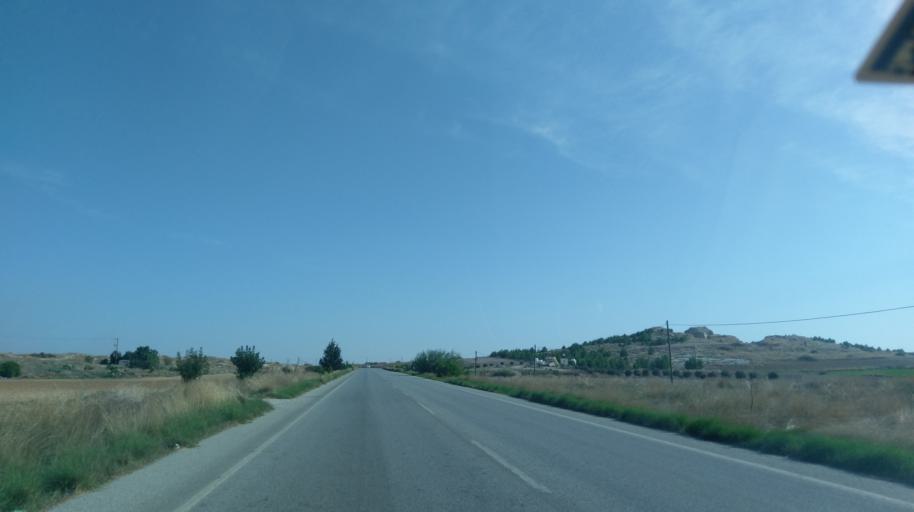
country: CY
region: Ammochostos
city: Lefkonoiko
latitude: 35.2512
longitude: 33.6255
